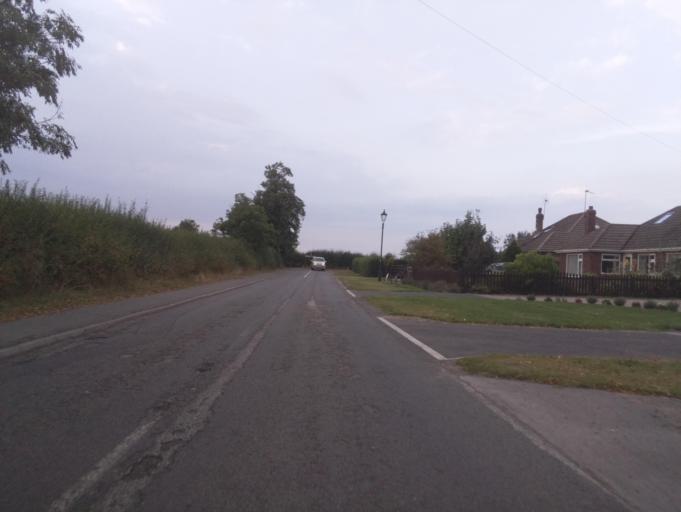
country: GB
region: England
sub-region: Lincolnshire
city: Skellingthorpe
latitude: 53.1329
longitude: -0.6382
